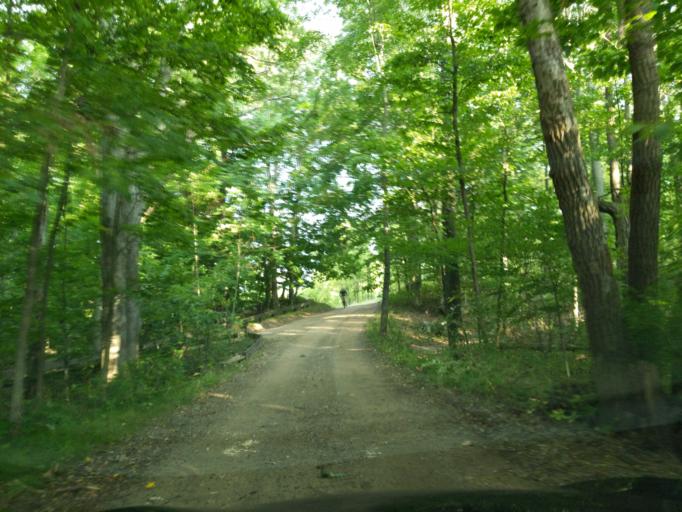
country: US
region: Michigan
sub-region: Eaton County
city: Dimondale
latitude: 42.5987
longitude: -84.5921
